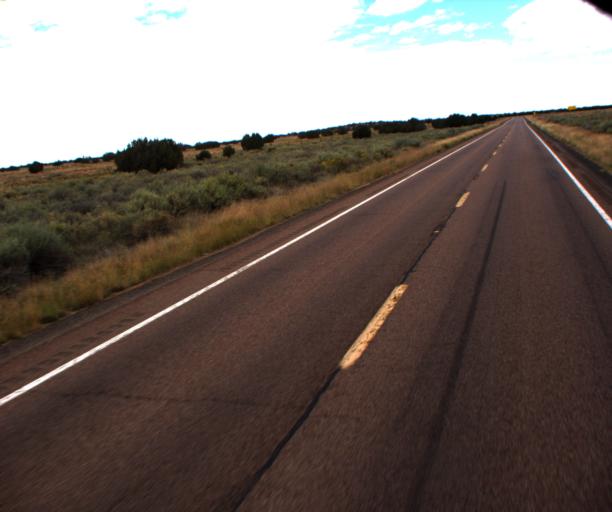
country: US
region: Arizona
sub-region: Navajo County
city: Heber-Overgaard
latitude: 34.5646
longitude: -110.4139
